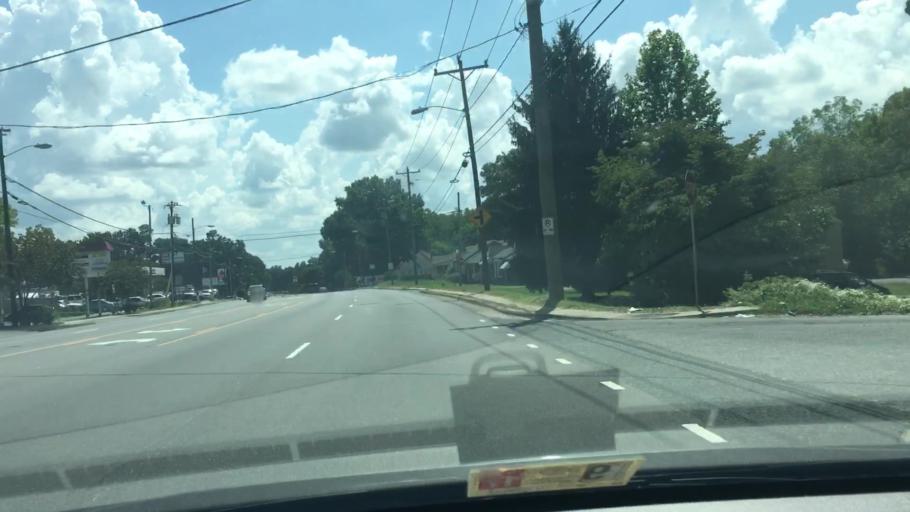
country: US
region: North Carolina
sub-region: Mecklenburg County
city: Charlotte
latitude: 35.2677
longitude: -80.7949
